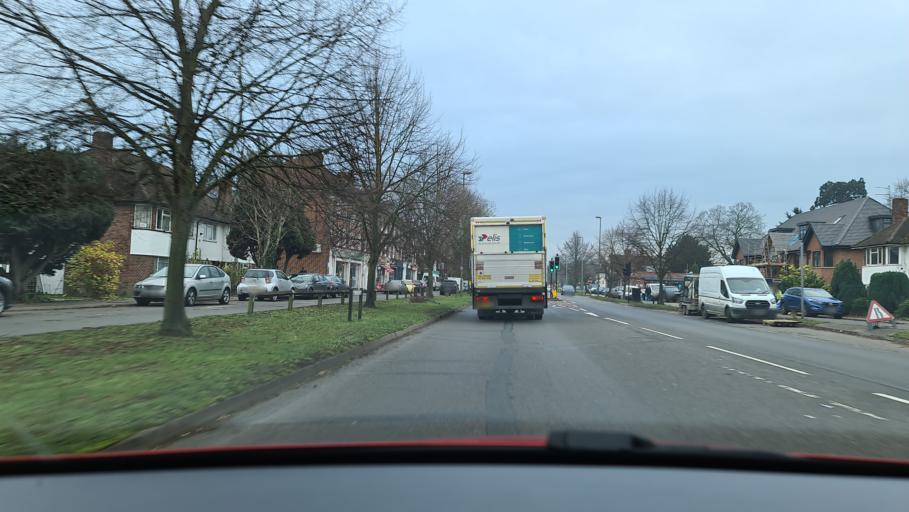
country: GB
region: England
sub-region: Surrey
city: Thames Ditton
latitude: 51.3853
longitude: -0.3468
